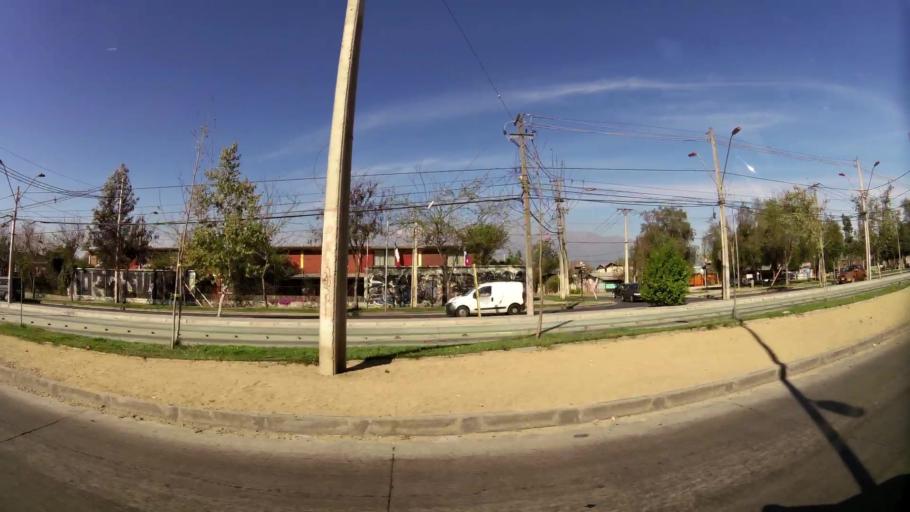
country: CL
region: Santiago Metropolitan
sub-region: Provincia de Santiago
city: Santiago
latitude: -33.4917
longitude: -70.6295
